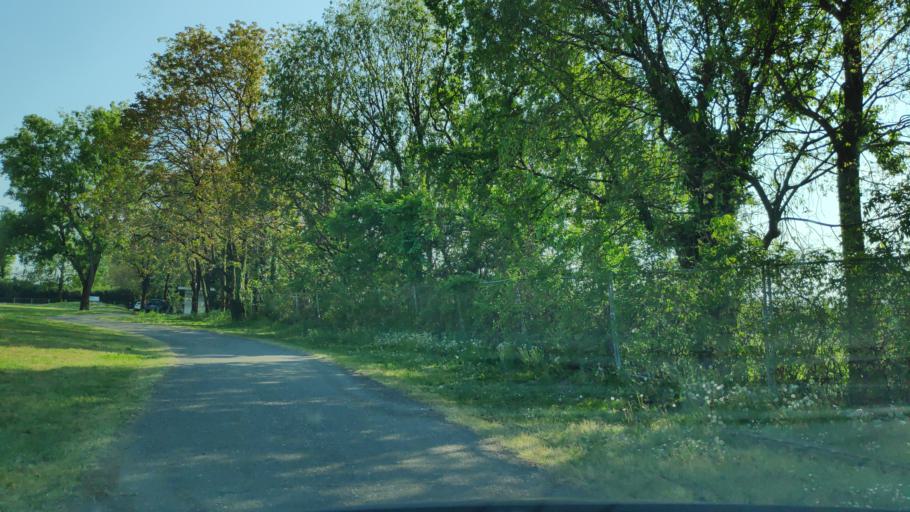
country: IT
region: Lombardy
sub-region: Citta metropolitana di Milano
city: Novegro-Tregarezzo-San Felice
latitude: 45.4698
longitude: 9.2728
